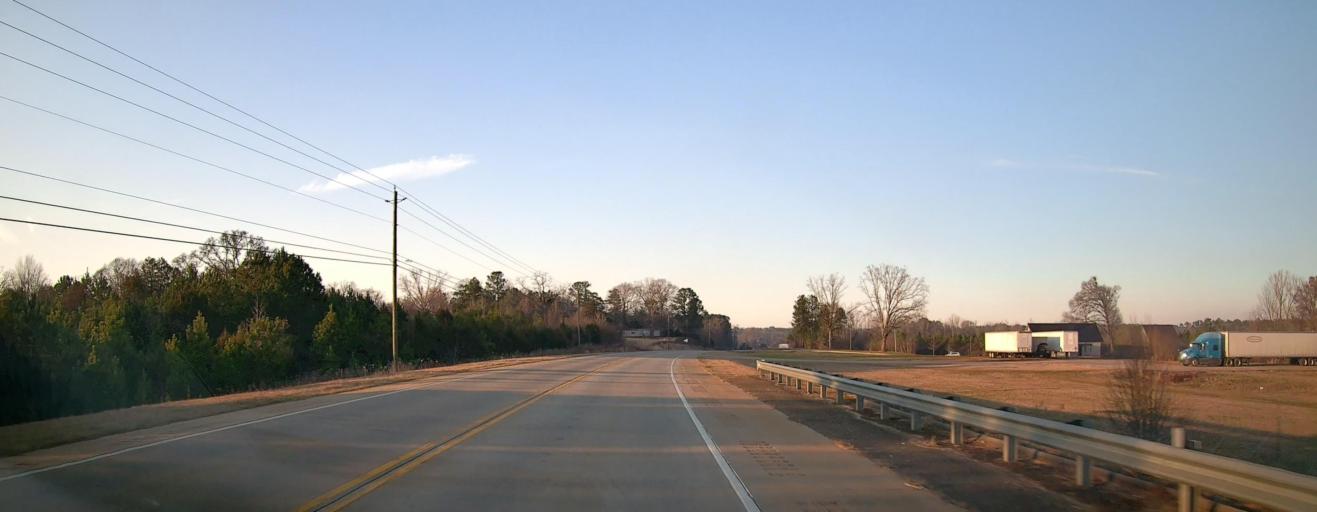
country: US
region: Georgia
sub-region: Troup County
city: La Grange
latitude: 33.0086
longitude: -85.0876
